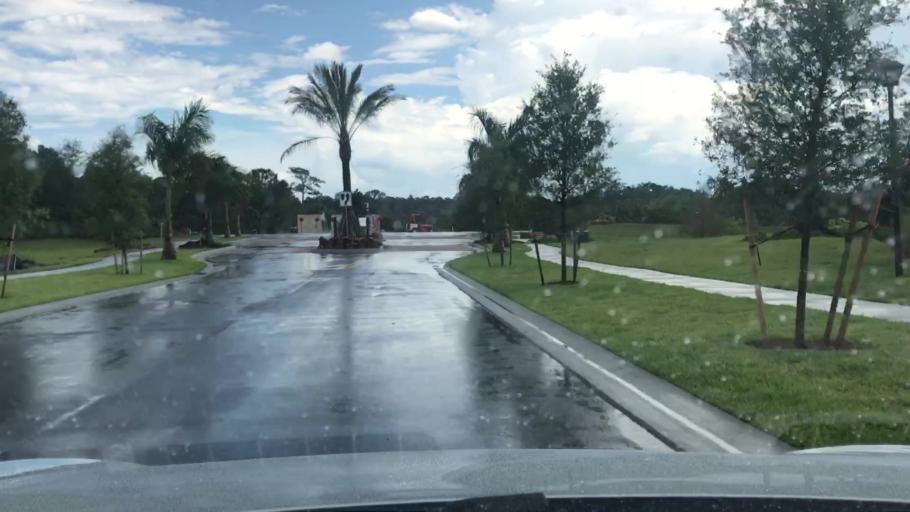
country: US
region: Florida
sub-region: Indian River County
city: Gifford
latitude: 27.6889
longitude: -80.4270
